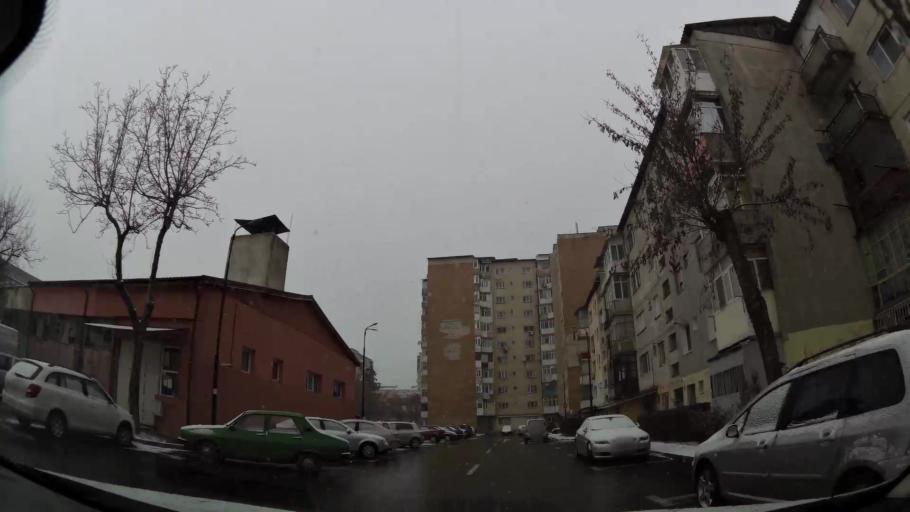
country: RO
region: Dambovita
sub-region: Municipiul Targoviste
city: Targoviste
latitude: 44.9296
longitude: 25.4488
